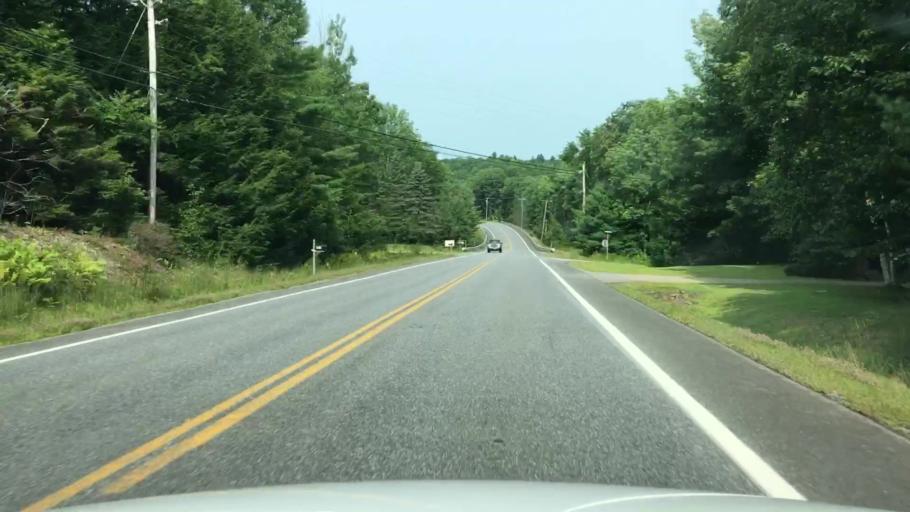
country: US
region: Maine
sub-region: Kennebec County
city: Winthrop
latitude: 44.3303
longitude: -70.0031
